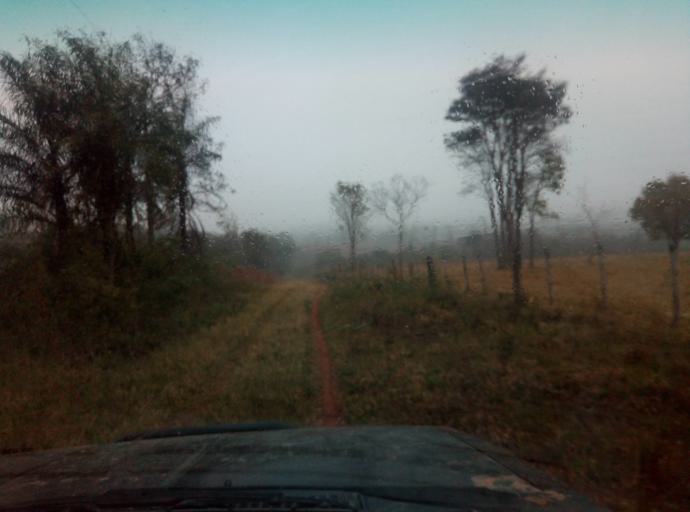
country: PY
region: Caaguazu
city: Doctor Cecilio Baez
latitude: -25.1510
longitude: -56.2606
